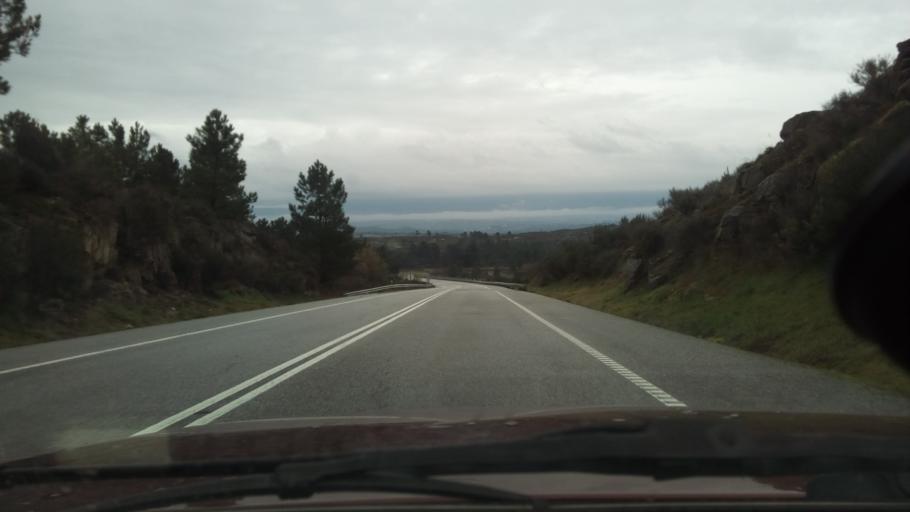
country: PT
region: Guarda
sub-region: Fornos de Algodres
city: Fornos de Algodres
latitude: 40.6041
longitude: -7.5837
